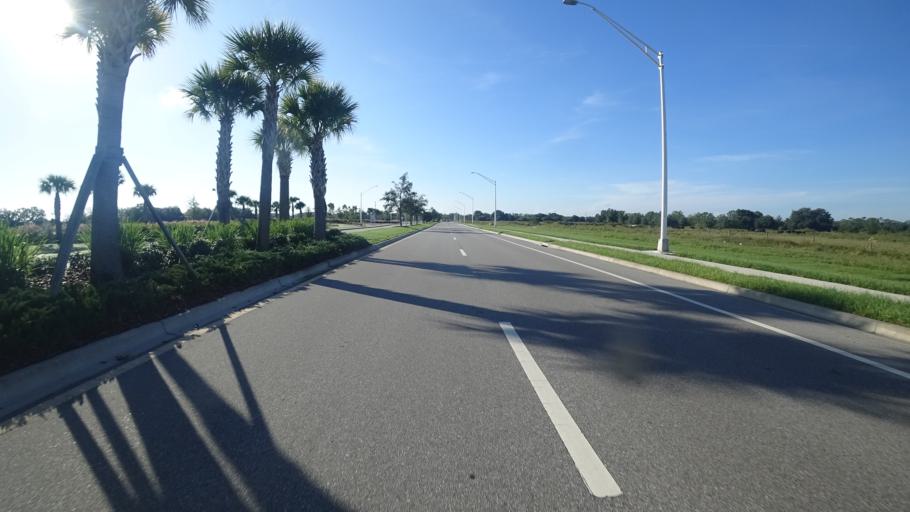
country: US
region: Florida
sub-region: Sarasota County
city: The Meadows
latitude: 27.4342
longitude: -82.3733
